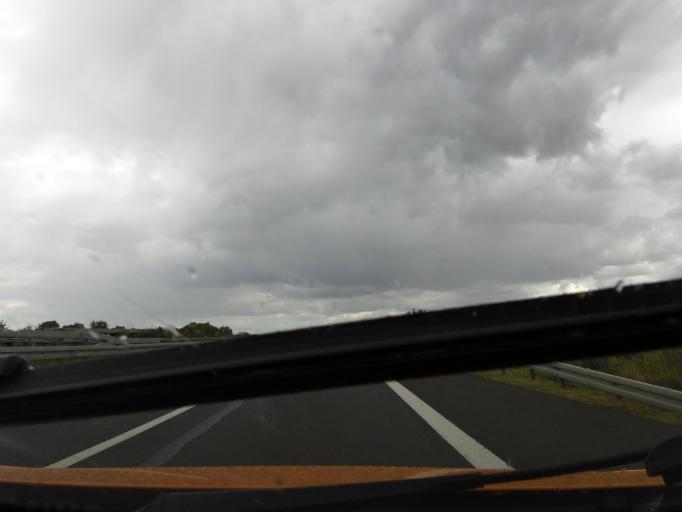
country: DE
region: Brandenburg
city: Gramzow
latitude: 53.2775
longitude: 14.0644
